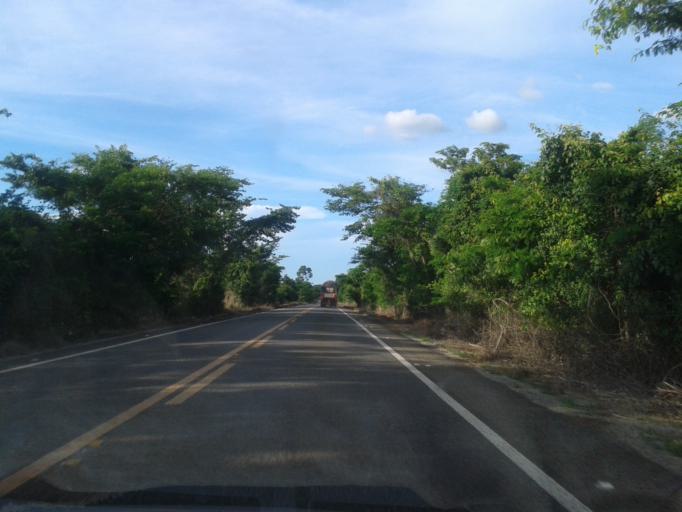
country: BR
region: Goias
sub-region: Sao Miguel Do Araguaia
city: Sao Miguel do Araguaia
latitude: -13.6943
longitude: -50.3316
